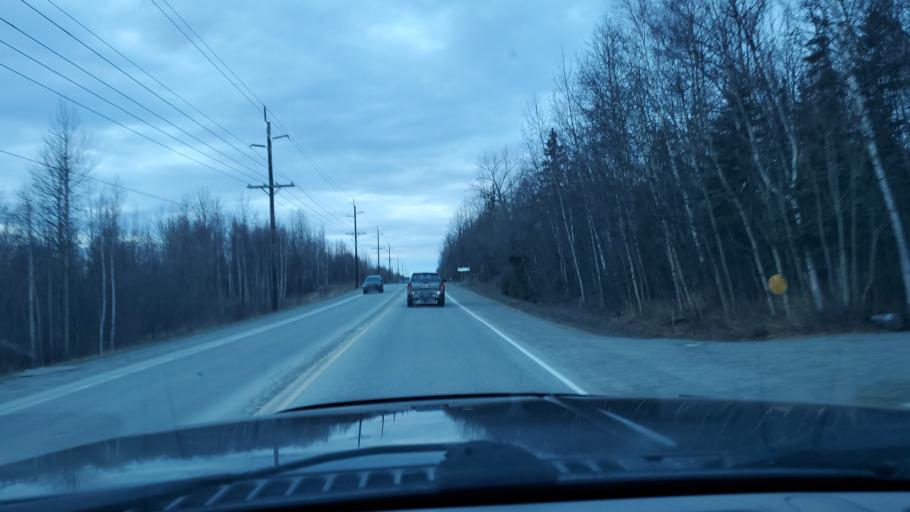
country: US
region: Alaska
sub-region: Matanuska-Susitna Borough
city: Lakes
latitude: 61.6139
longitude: -149.3098
